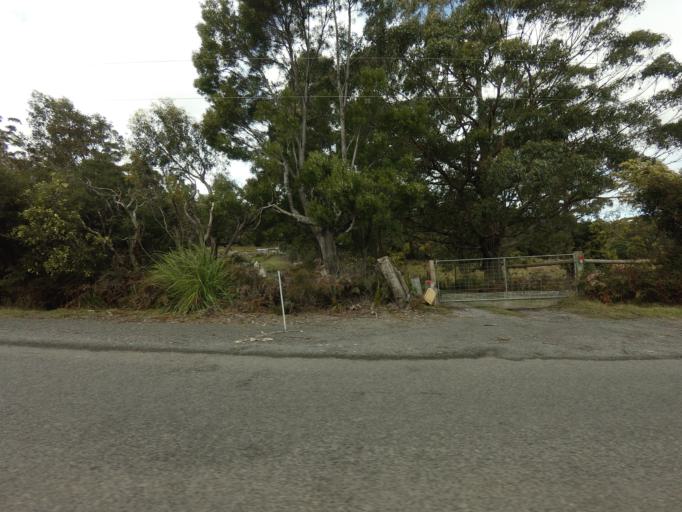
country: AU
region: Tasmania
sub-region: Huon Valley
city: Geeveston
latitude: -43.4170
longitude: 146.9089
